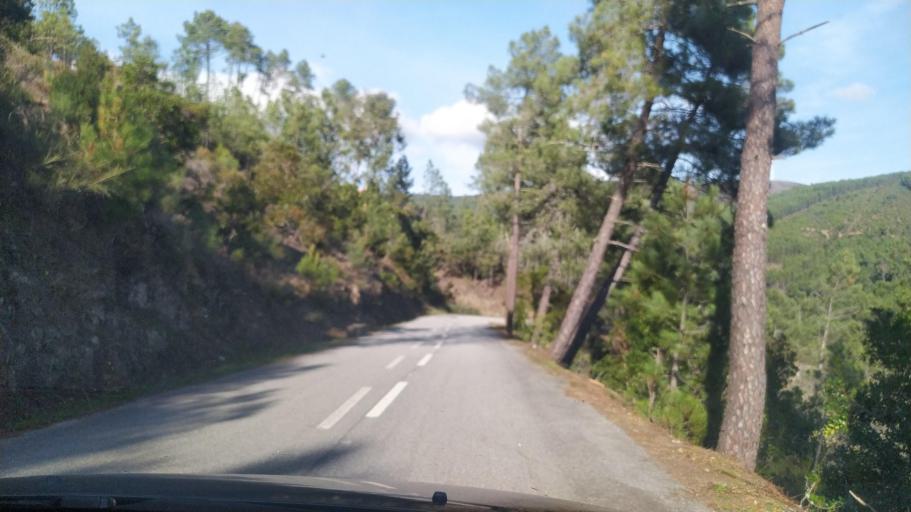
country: PT
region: Coimbra
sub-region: Oliveira do Hospital
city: Oliveira do Hospital
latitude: 40.2041
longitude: -7.7346
